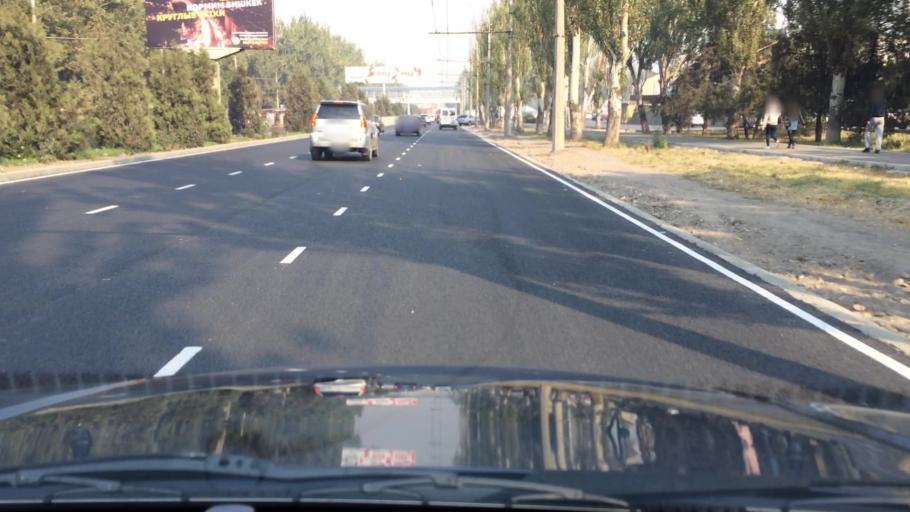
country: KG
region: Chuy
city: Lebedinovka
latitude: 42.8694
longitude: 74.6368
